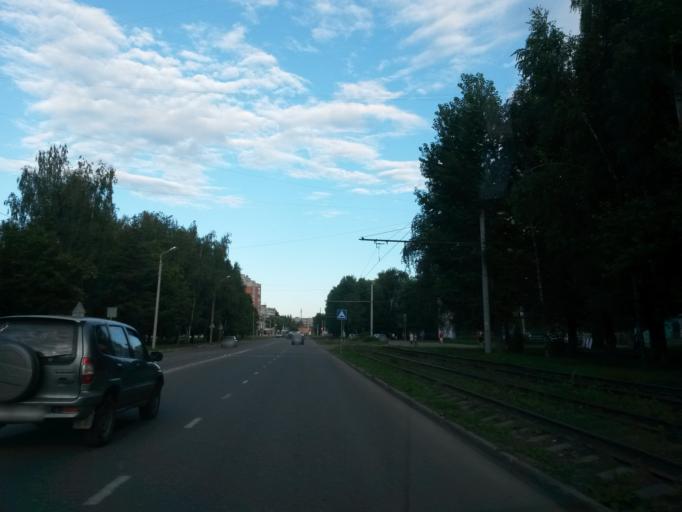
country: RU
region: Jaroslavl
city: Yaroslavl
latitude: 57.6818
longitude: 39.7743
